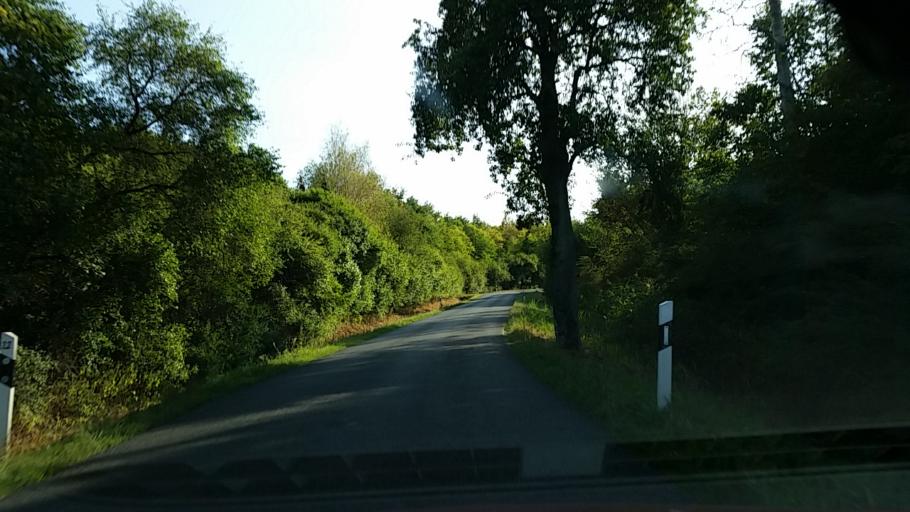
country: DE
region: Lower Saxony
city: Lehre
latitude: 52.3401
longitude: 10.6974
